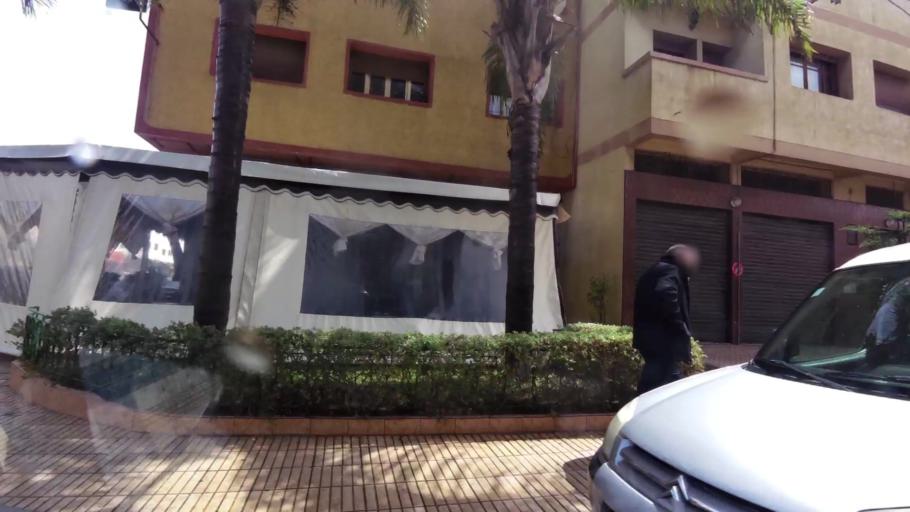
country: MA
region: Grand Casablanca
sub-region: Casablanca
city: Casablanca
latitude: 33.5522
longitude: -7.6788
